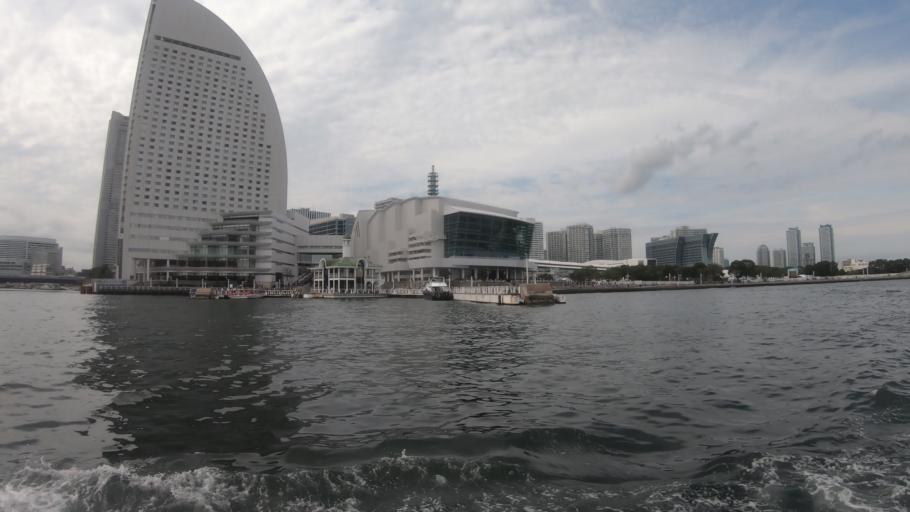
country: JP
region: Kanagawa
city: Yokohama
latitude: 35.4584
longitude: 139.6400
